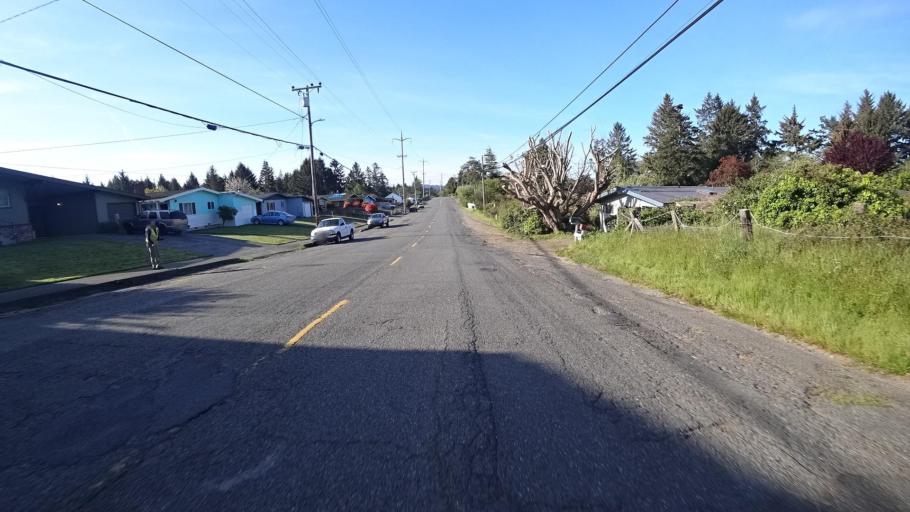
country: US
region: California
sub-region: Humboldt County
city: Bayview
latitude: 40.7627
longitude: -124.1779
